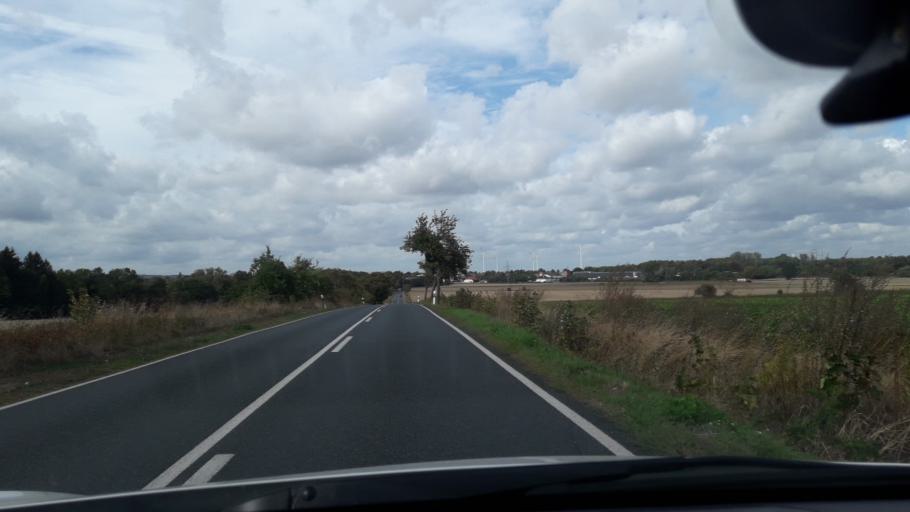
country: DE
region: Lower Saxony
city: Alt Wallmoden
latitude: 52.0298
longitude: 10.3355
